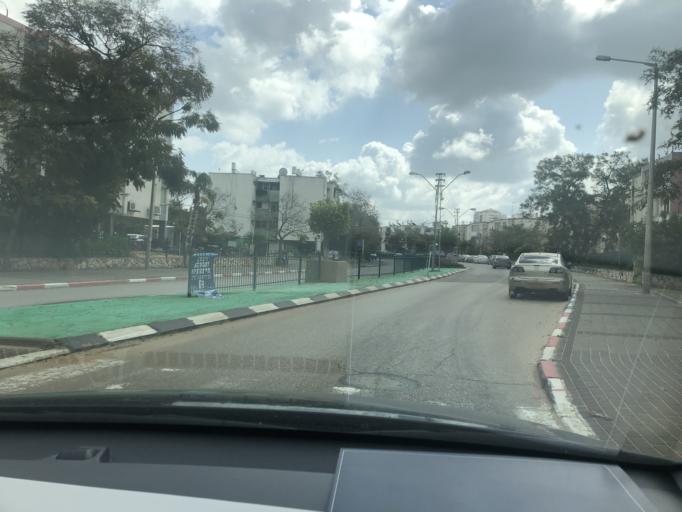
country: IL
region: Haifa
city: Hadera
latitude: 32.4733
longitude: 34.9522
